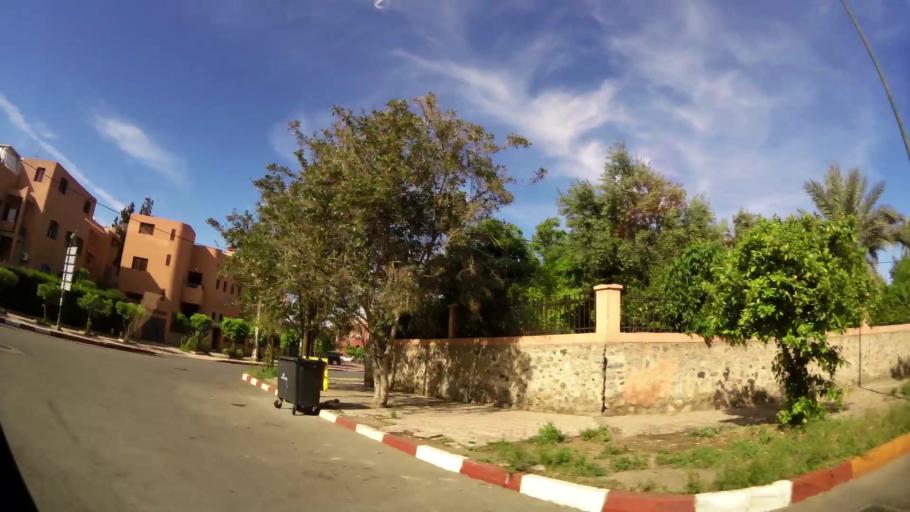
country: MA
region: Marrakech-Tensift-Al Haouz
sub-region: Marrakech
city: Marrakesh
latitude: 31.6512
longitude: -8.0057
